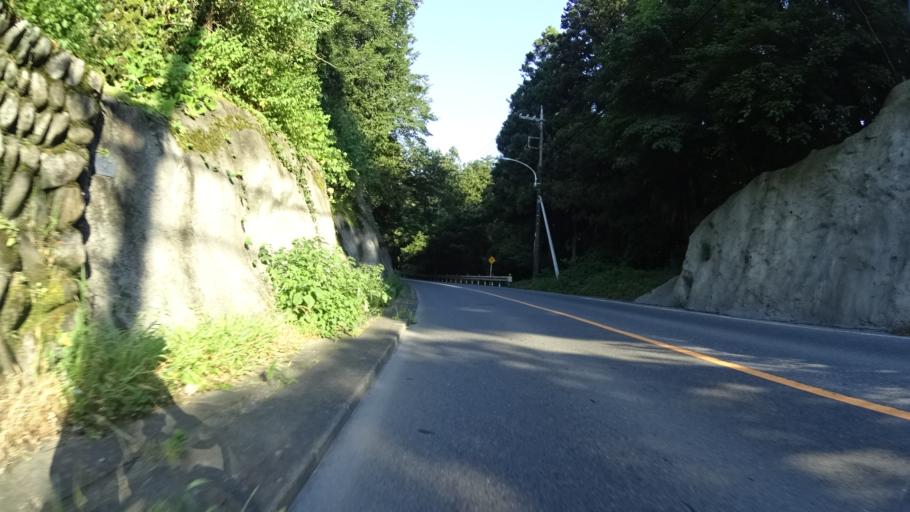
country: JP
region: Tokyo
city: Ome
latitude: 35.8046
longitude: 139.1742
